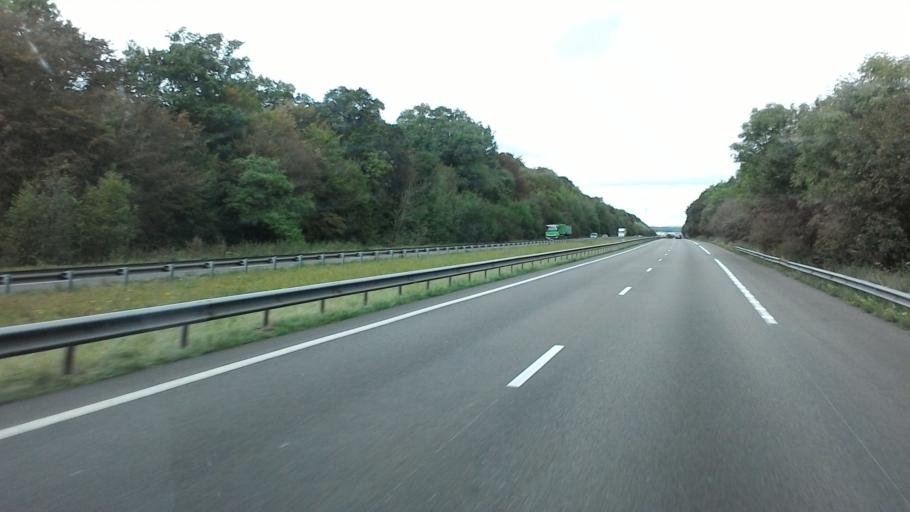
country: FR
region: Lorraine
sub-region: Departement de Meurthe-et-Moselle
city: Pont-a-Mousson
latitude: 48.9160
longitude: 6.1099
